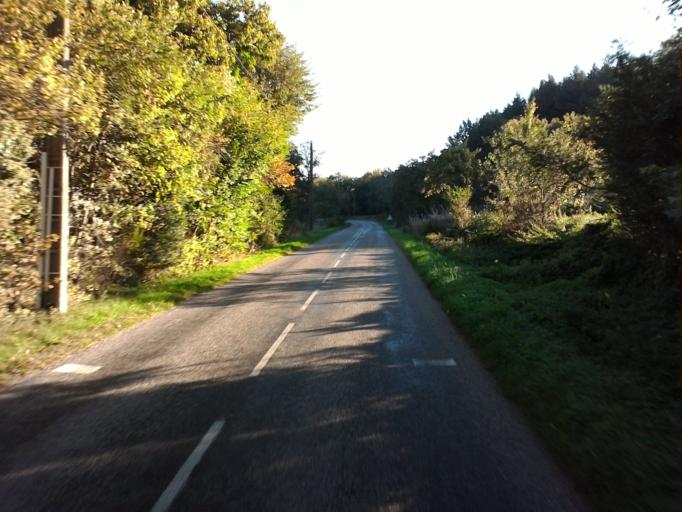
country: FR
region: Bourgogne
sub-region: Departement de la Cote-d'Or
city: Saulieu
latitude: 47.2724
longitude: 4.1228
